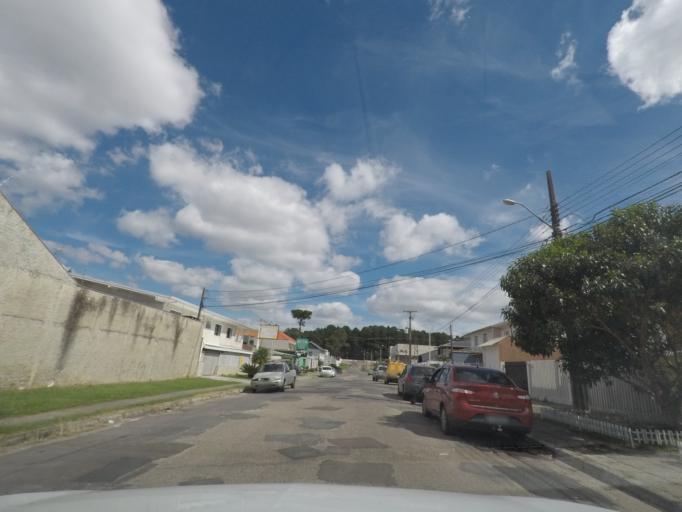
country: BR
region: Parana
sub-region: Sao Jose Dos Pinhais
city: Sao Jose dos Pinhais
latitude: -25.5077
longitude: -49.2320
